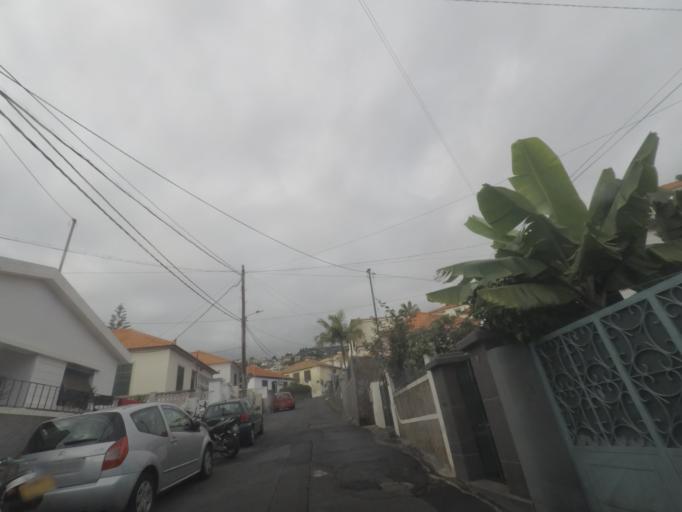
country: PT
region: Madeira
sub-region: Funchal
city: Nossa Senhora do Monte
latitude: 32.6554
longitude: -16.9029
